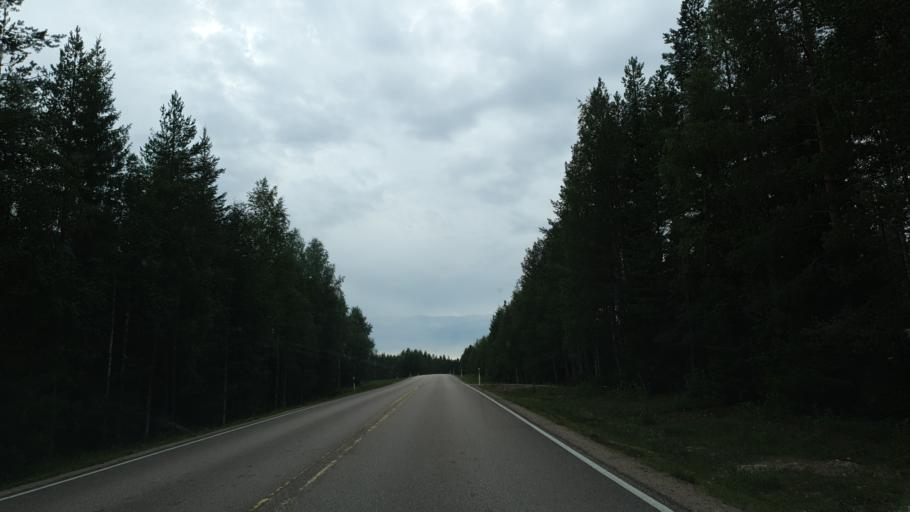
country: FI
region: Kainuu
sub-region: Kehys-Kainuu
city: Kuhmo
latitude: 64.4319
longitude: 29.1235
